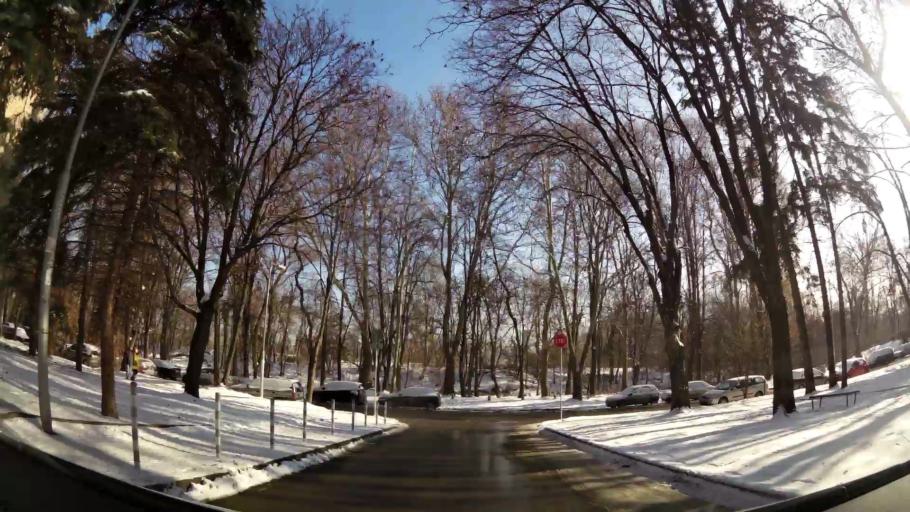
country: BG
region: Sofia-Capital
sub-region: Stolichna Obshtina
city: Sofia
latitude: 42.6785
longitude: 23.3128
